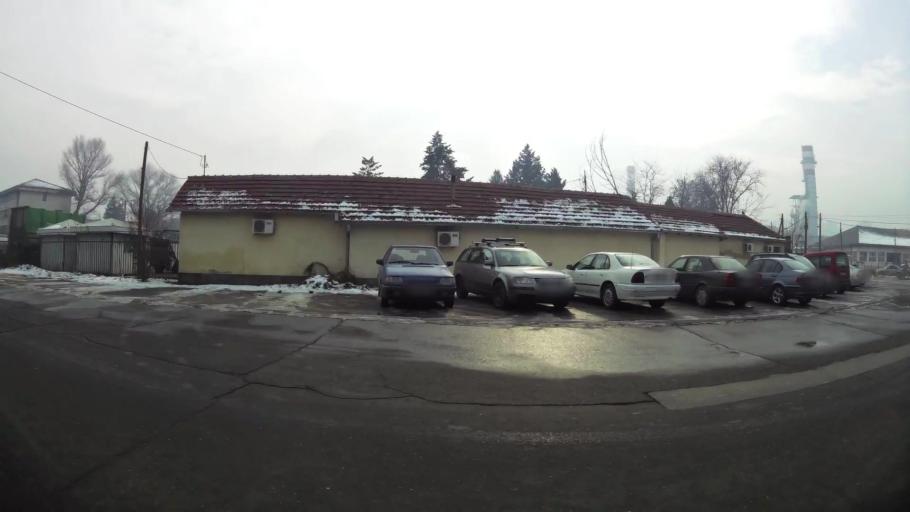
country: MK
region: Karpos
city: Skopje
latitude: 41.9966
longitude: 21.4542
